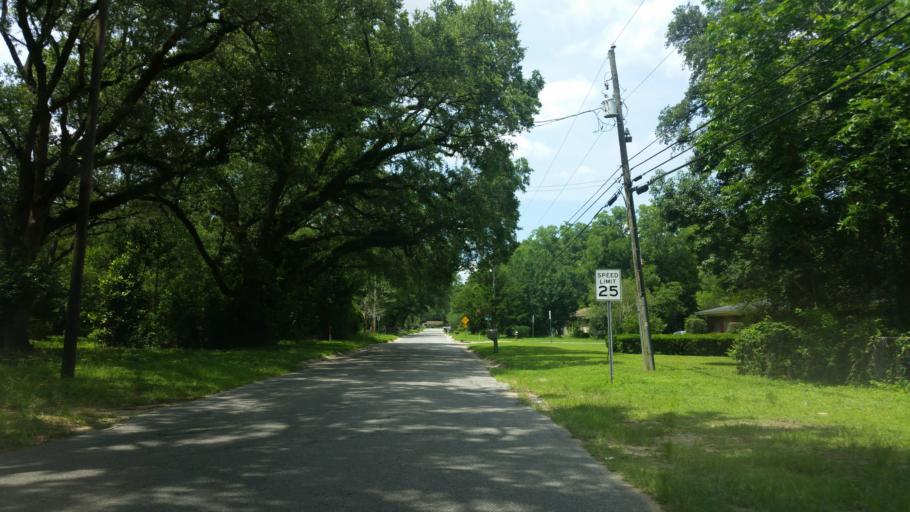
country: US
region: Florida
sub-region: Escambia County
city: Ensley
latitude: 30.5145
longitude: -87.2540
